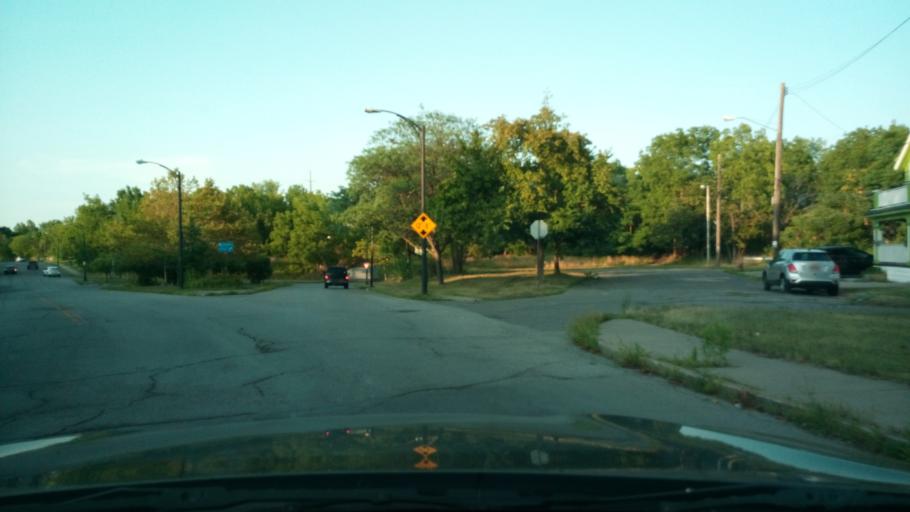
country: US
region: New York
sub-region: Erie County
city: Kenmore
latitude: 42.9353
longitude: -78.8994
